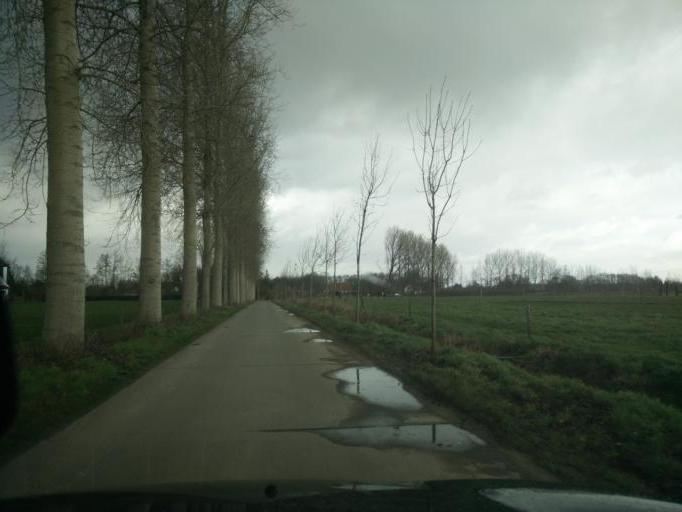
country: BE
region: Flanders
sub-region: Provincie Oost-Vlaanderen
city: Laarne
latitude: 51.0458
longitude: 3.8347
